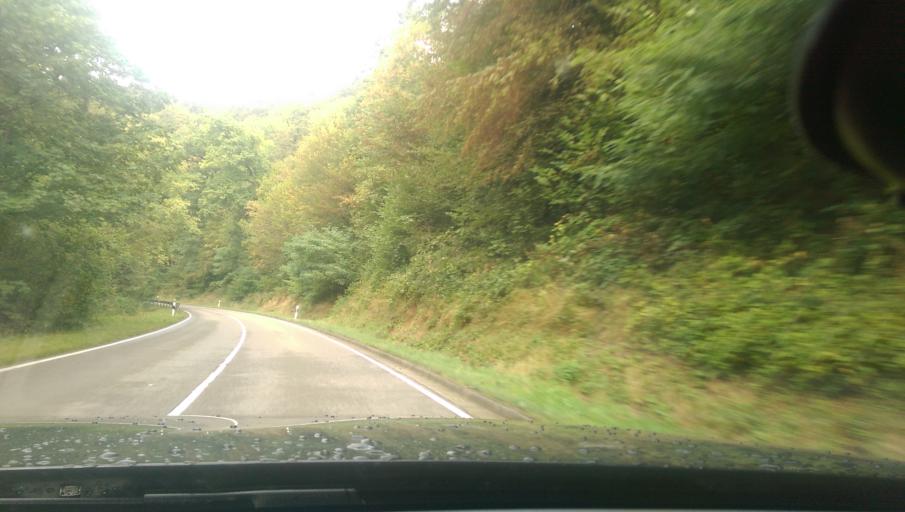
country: DE
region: Baden-Wuerttemberg
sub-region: Karlsruhe Region
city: Unterreichenbach
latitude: 48.8610
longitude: 8.7433
